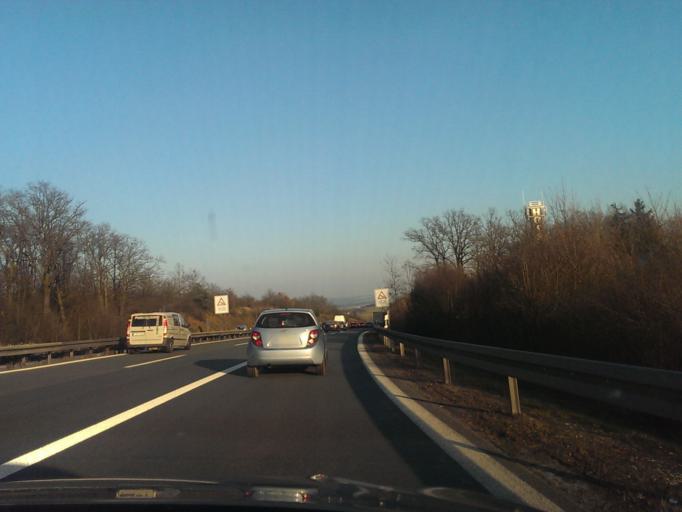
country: DE
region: Saxony
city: Weischlitz
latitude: 50.4353
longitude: 12.0942
